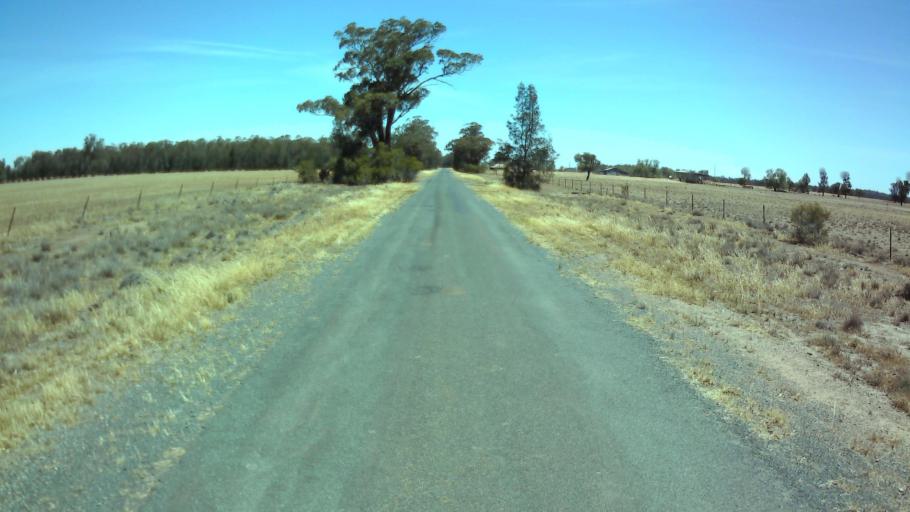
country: AU
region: New South Wales
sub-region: Weddin
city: Grenfell
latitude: -33.9004
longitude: 147.6865
